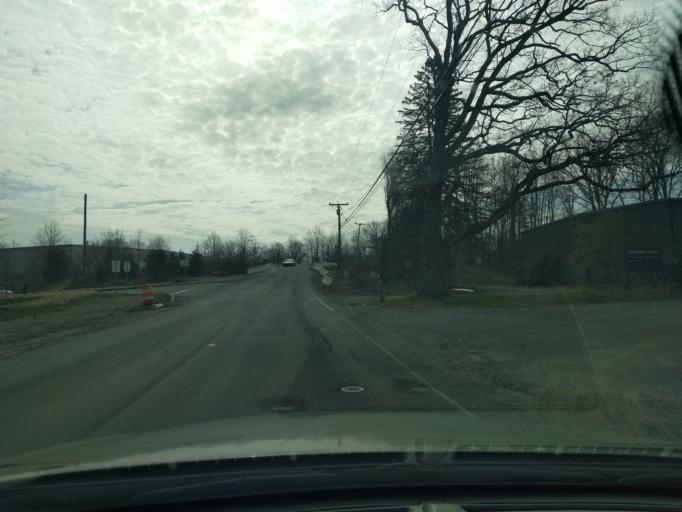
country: US
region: Connecticut
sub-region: Fairfield County
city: Newtown
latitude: 41.3466
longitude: -73.2520
